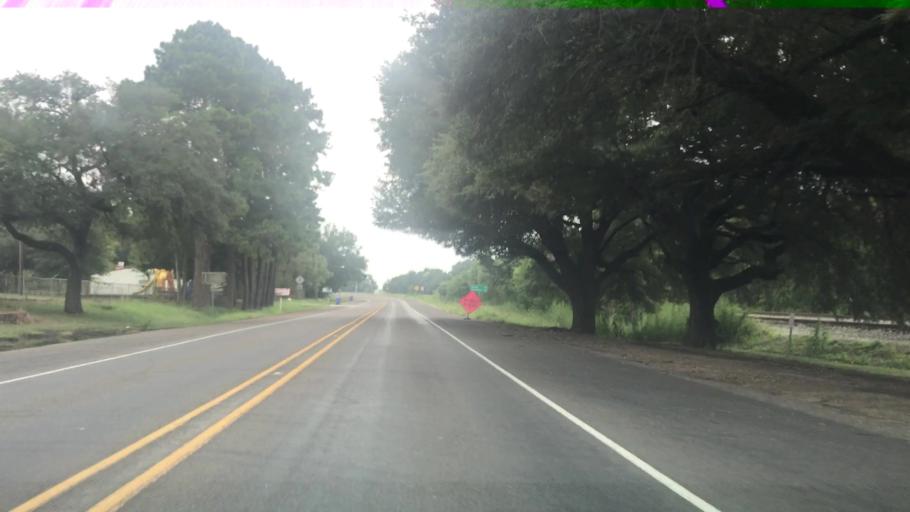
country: US
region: Texas
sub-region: Houston County
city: Cooper
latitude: 31.1244
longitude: -95.4452
